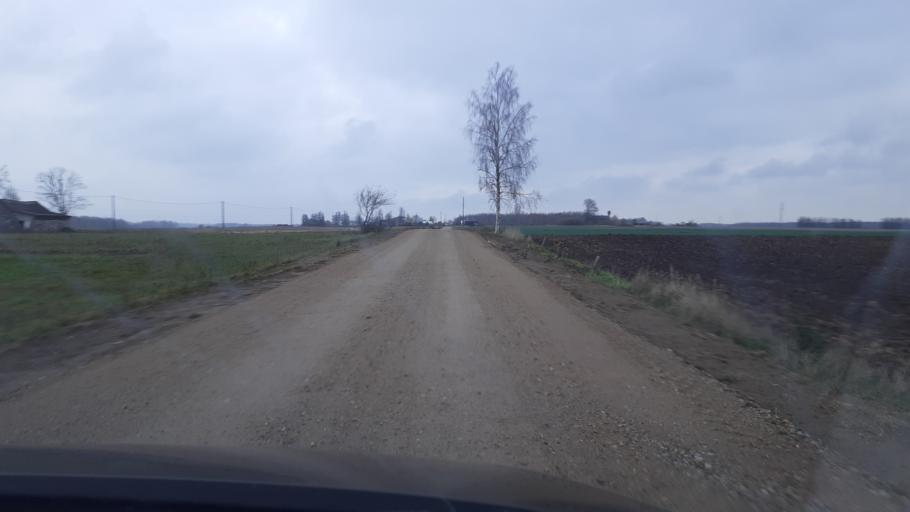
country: LV
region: Talsu Rajons
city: Sabile
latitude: 56.9357
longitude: 22.4180
